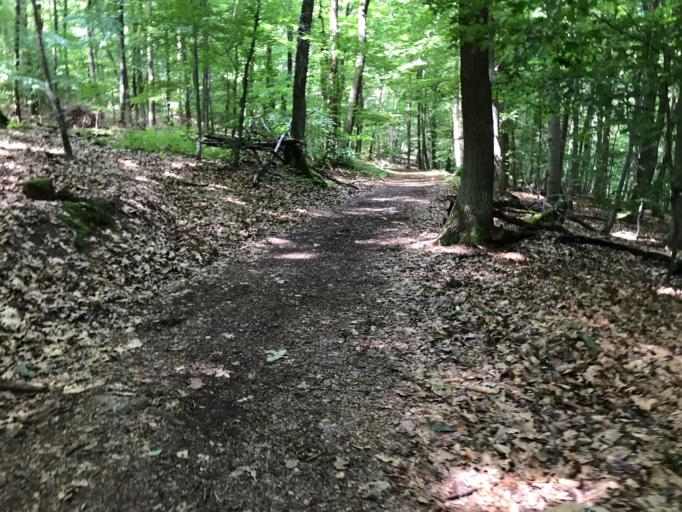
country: DE
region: Rheinland-Pfalz
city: Weiler
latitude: 49.9704
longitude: 7.8693
